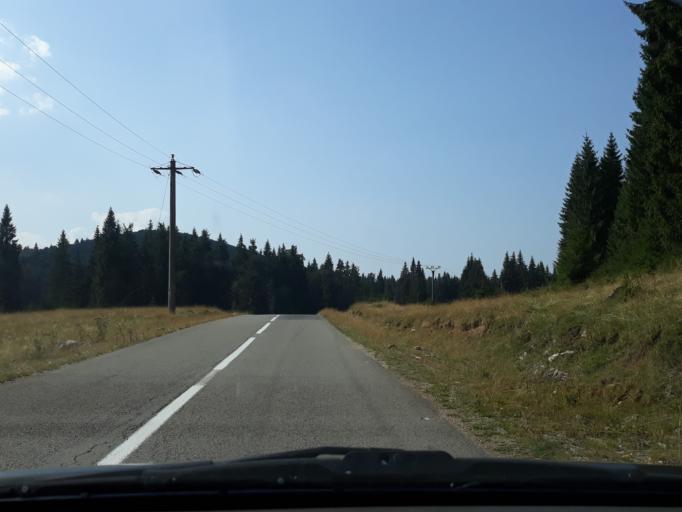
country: RO
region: Alba
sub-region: Comuna Arieseni
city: Arieseni
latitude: 46.5989
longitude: 22.7097
